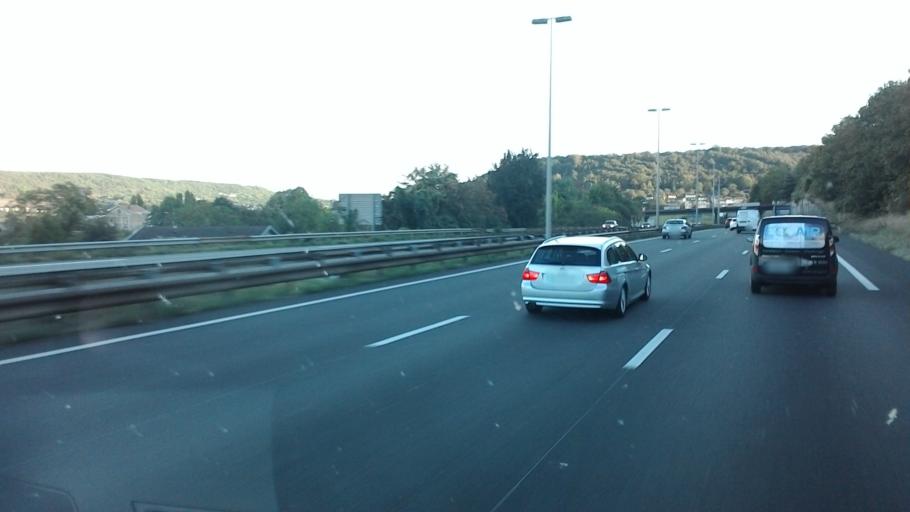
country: FR
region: Lorraine
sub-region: Departement de Meurthe-et-Moselle
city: Champigneulles
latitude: 48.7346
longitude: 6.1574
